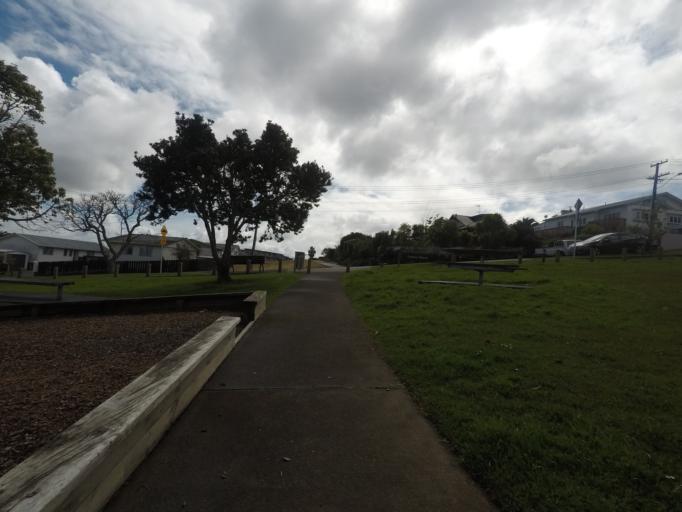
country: NZ
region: Auckland
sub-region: Auckland
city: Rosebank
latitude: -36.9009
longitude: 174.6992
